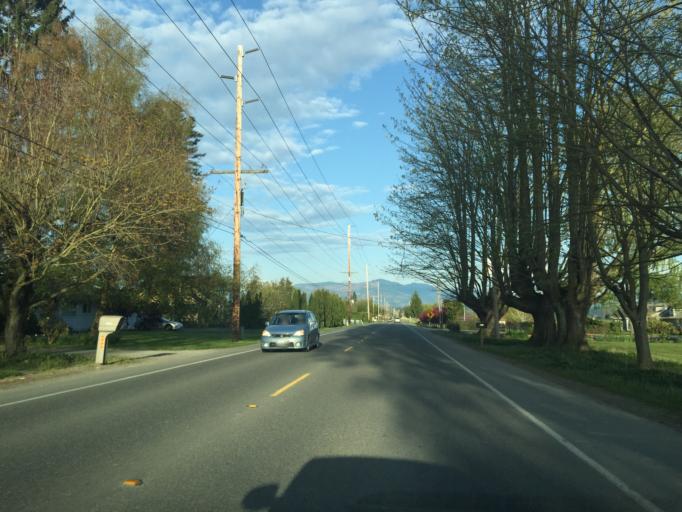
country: US
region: Washington
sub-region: Skagit County
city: Mount Vernon
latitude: 48.4209
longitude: -122.3882
